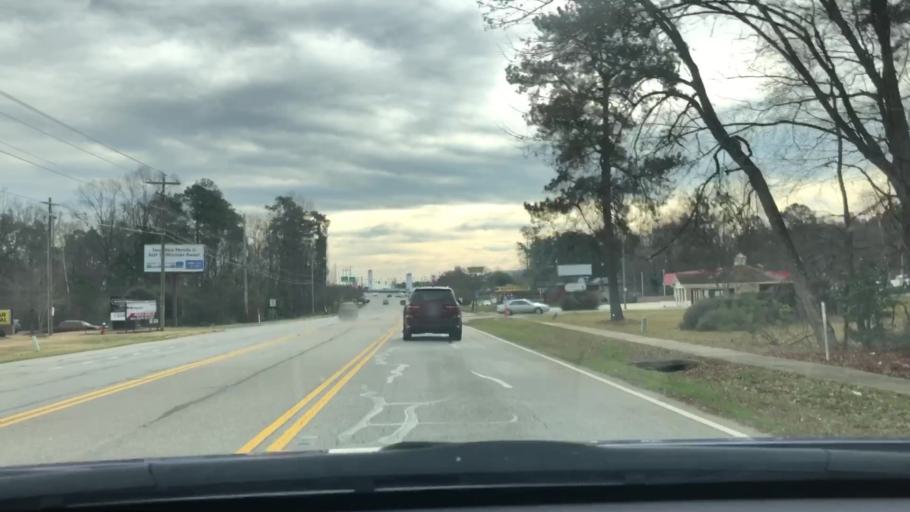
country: US
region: South Carolina
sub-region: Lexington County
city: Irmo
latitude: 34.1019
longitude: -81.1815
